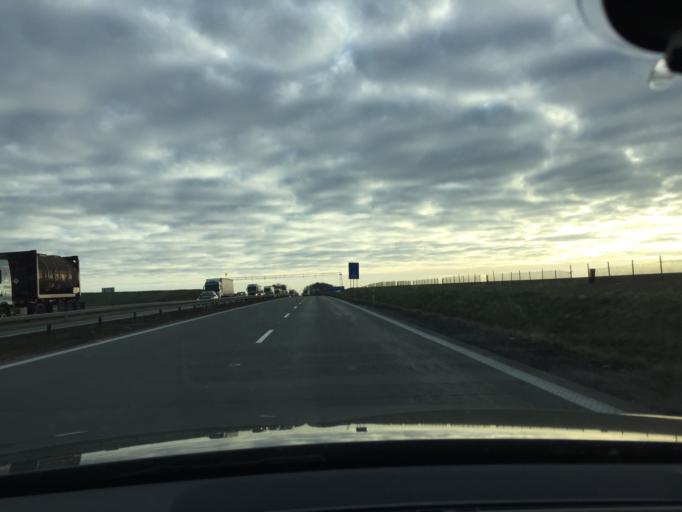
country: PL
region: Lower Silesian Voivodeship
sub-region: Powiat legnicki
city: Legnickie Pole
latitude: 51.1353
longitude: 16.2944
